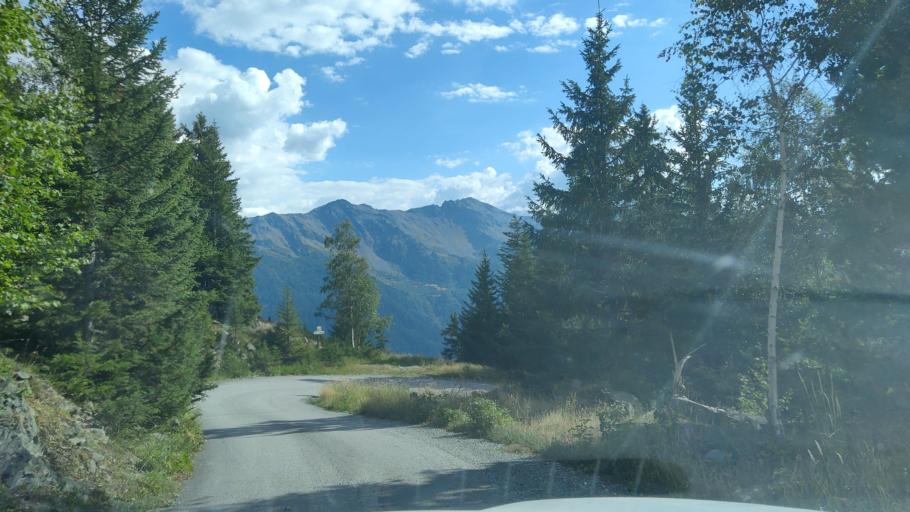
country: FR
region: Rhone-Alpes
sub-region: Departement de la Savoie
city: Val Thorens
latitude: 45.2268
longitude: 6.5590
